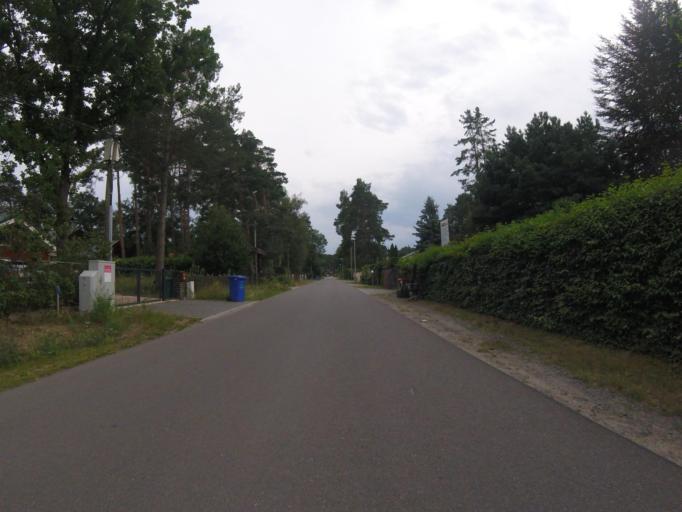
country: DE
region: Brandenburg
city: Gross Koris
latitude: 52.1681
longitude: 13.6976
